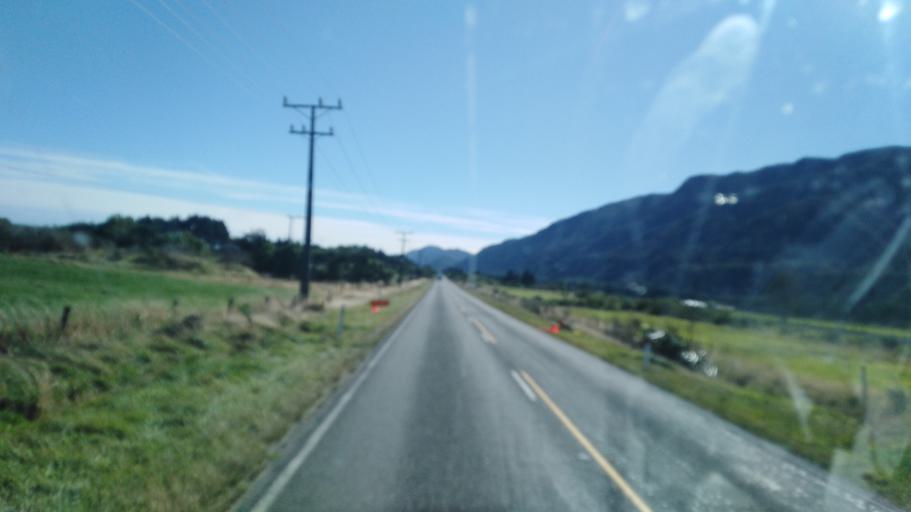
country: NZ
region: West Coast
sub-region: Buller District
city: Westport
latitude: -41.6646
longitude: 171.8118
